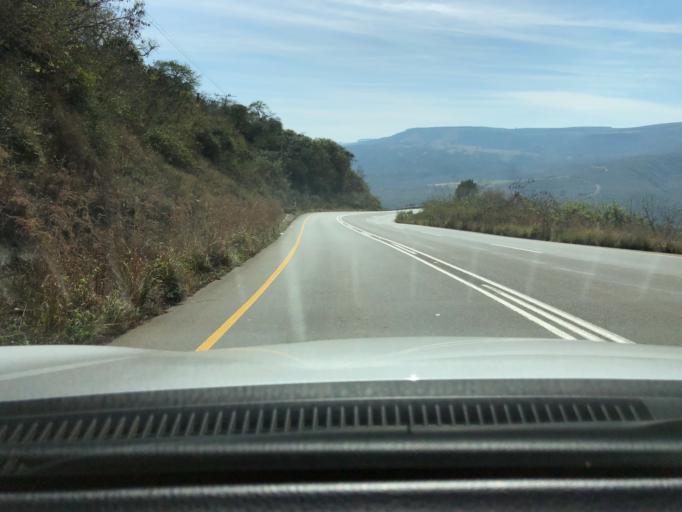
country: ZA
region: KwaZulu-Natal
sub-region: uMgungundlovu District Municipality
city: Richmond
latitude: -29.9893
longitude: 30.2469
